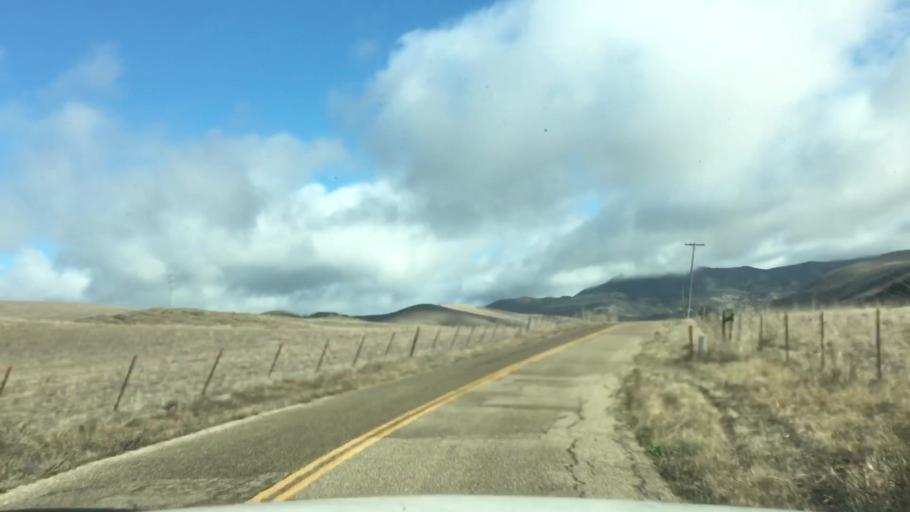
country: US
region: California
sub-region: San Luis Obispo County
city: Morro Bay
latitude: 35.3714
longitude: -120.8014
